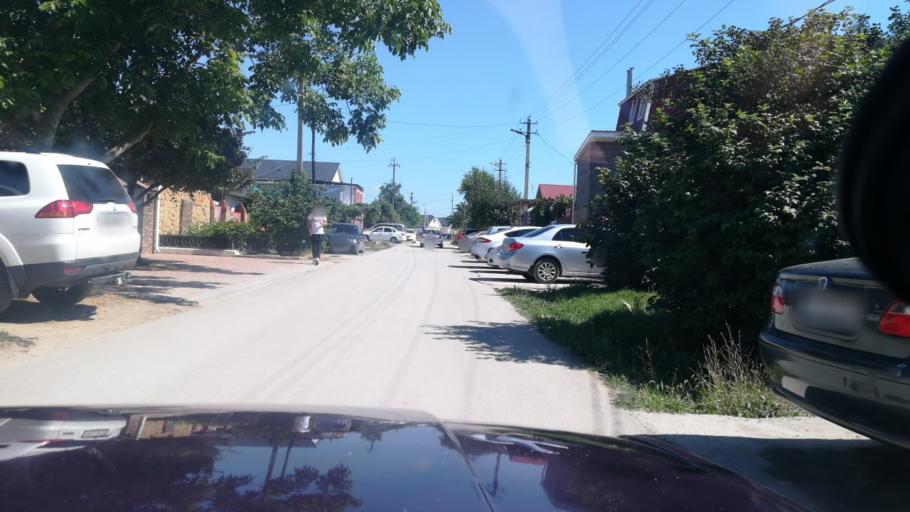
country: RU
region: Krasnodarskiy
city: Vityazevo
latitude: 44.9930
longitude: 37.2743
